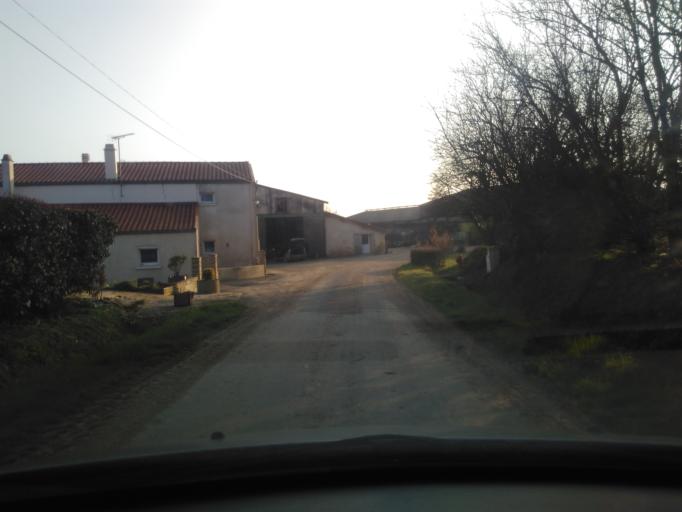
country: FR
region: Pays de la Loire
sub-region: Departement de la Vendee
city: Chantonnay
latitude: 46.6667
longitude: -1.0317
